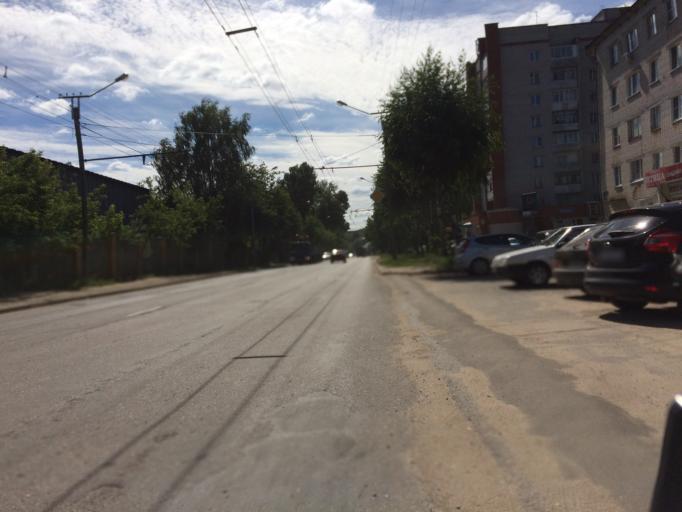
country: RU
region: Mariy-El
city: Yoshkar-Ola
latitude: 56.6375
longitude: 47.9474
